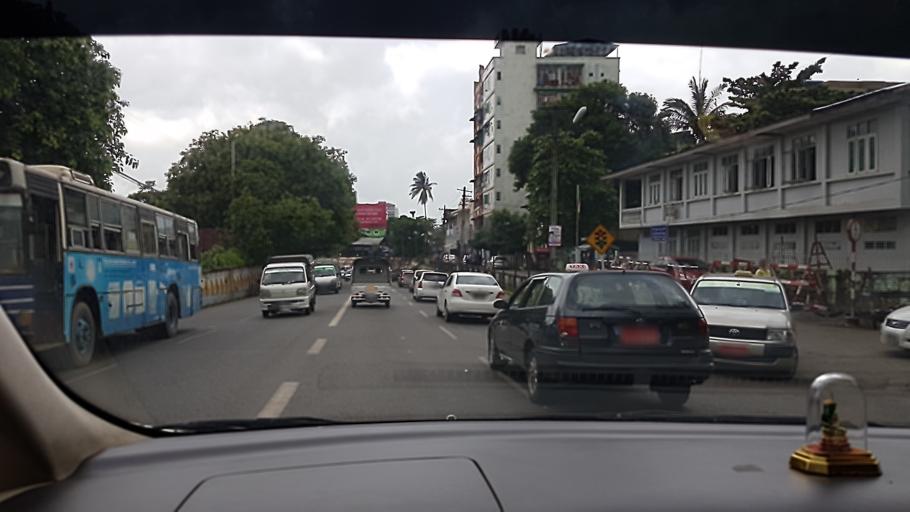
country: MM
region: Yangon
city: Yangon
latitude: 16.8053
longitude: 96.1258
